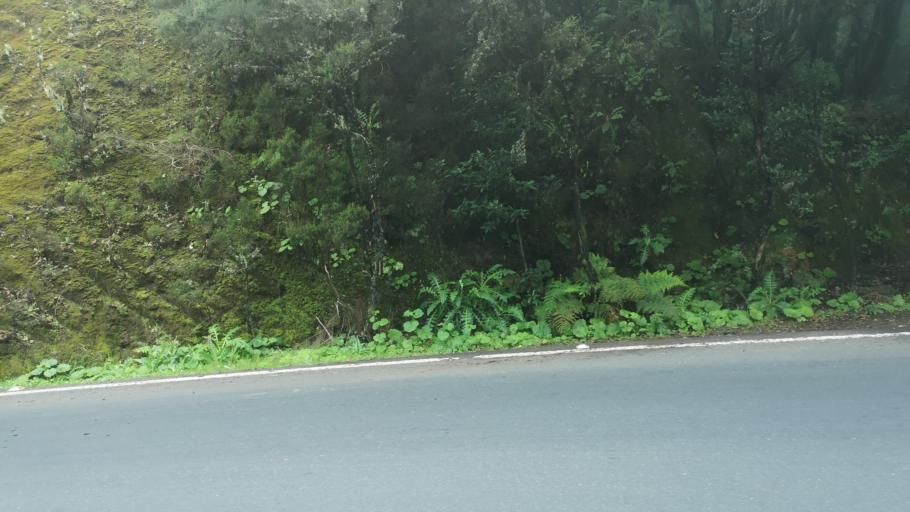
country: ES
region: Canary Islands
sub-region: Provincia de Santa Cruz de Tenerife
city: Alajero
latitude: 28.1098
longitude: -17.2247
